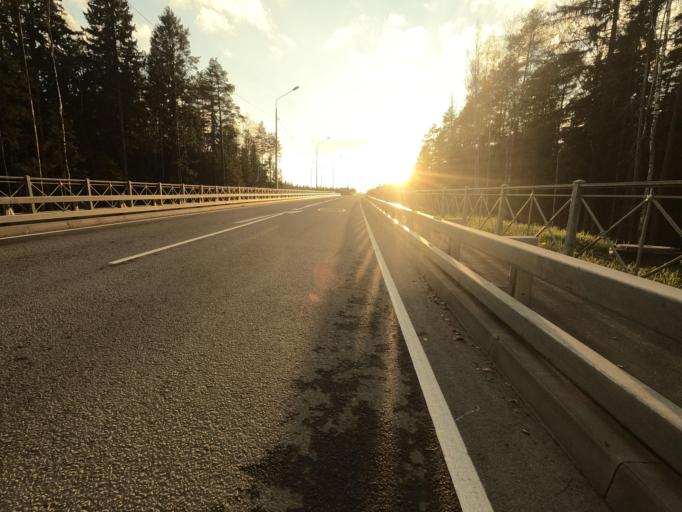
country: RU
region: St.-Petersburg
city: Beloostrov
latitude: 60.1711
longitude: 29.9764
